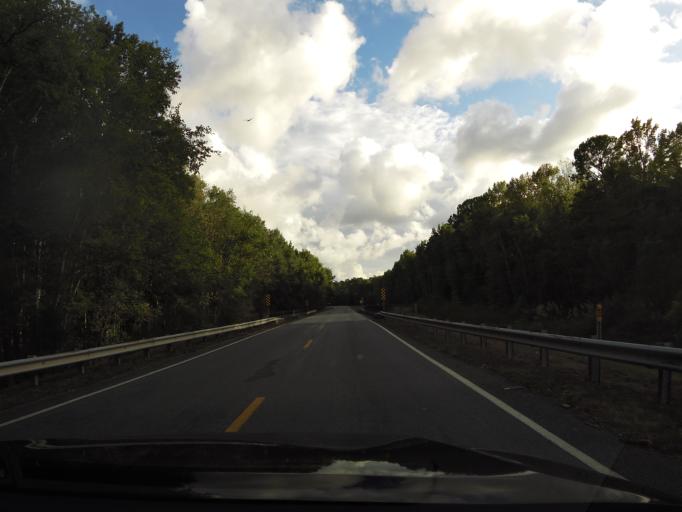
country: US
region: Georgia
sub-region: Liberty County
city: Midway
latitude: 31.7122
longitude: -81.4168
